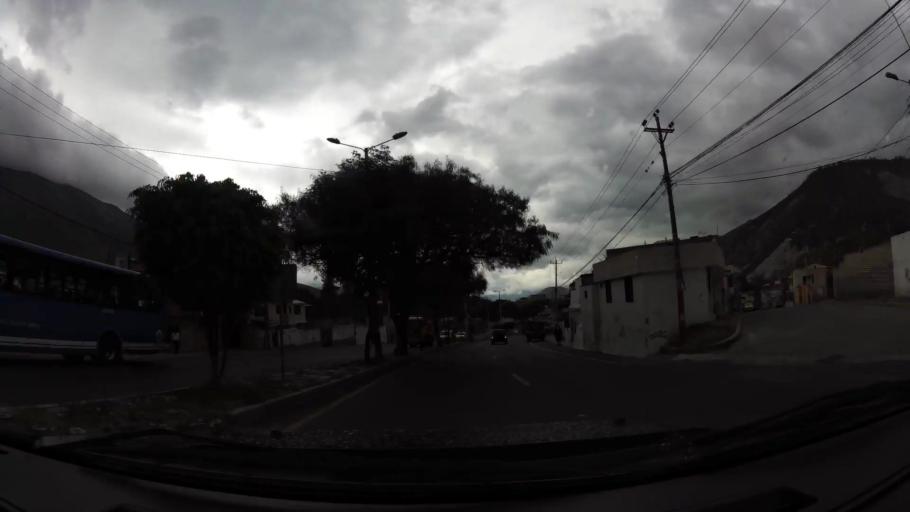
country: EC
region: Pichincha
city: Quito
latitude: -0.0595
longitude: -78.4562
